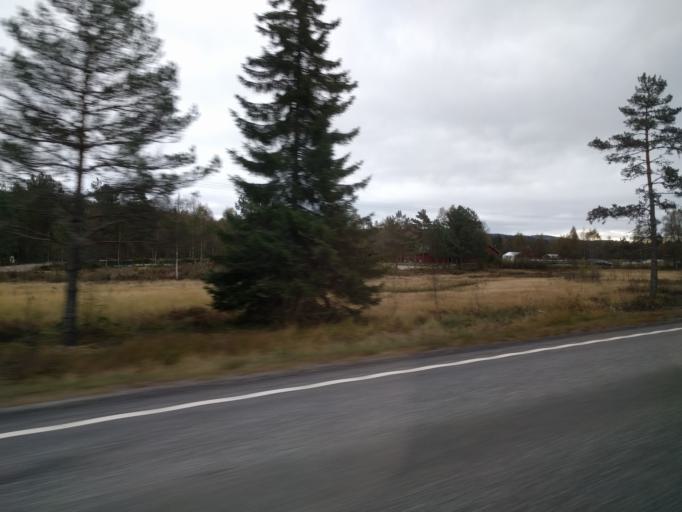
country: NO
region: Aust-Agder
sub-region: Evje og Hornnes
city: Evje
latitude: 58.5322
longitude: 7.7799
